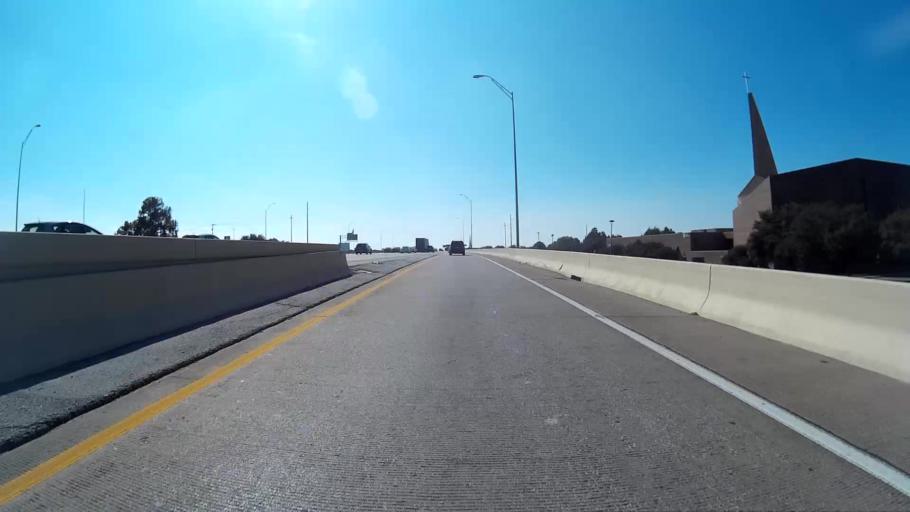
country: US
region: Texas
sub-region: Dallas County
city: Richardson
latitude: 32.9630
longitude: -96.7256
